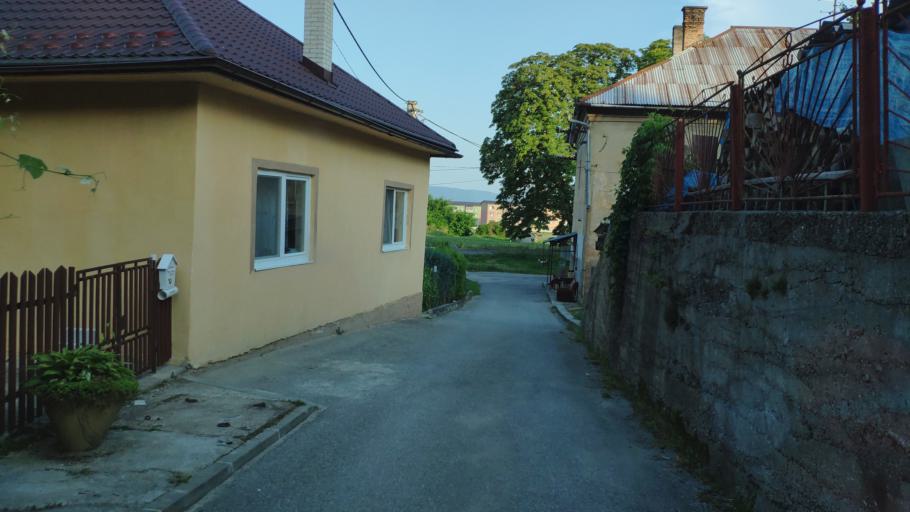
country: SK
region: Kosicky
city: Dobsina
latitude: 48.7208
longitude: 20.2704
